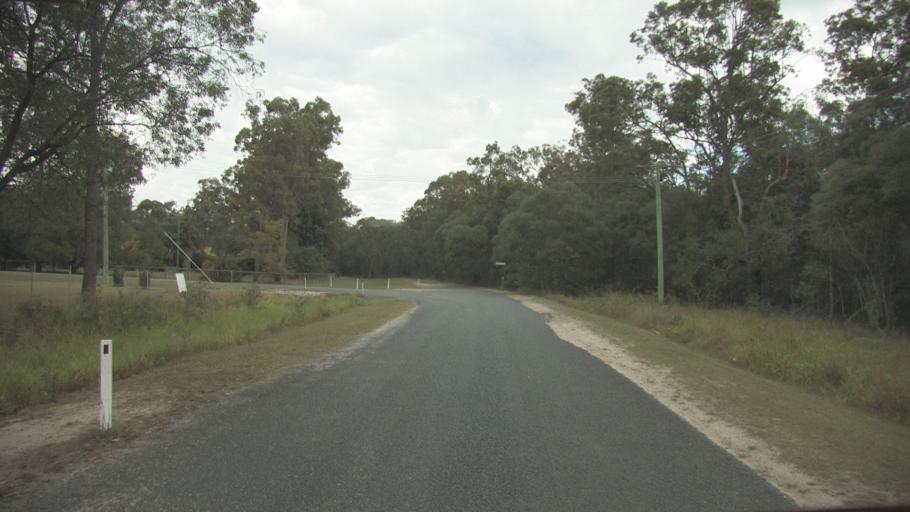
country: AU
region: Queensland
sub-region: Logan
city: Chambers Flat
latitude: -27.7863
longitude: 153.1087
